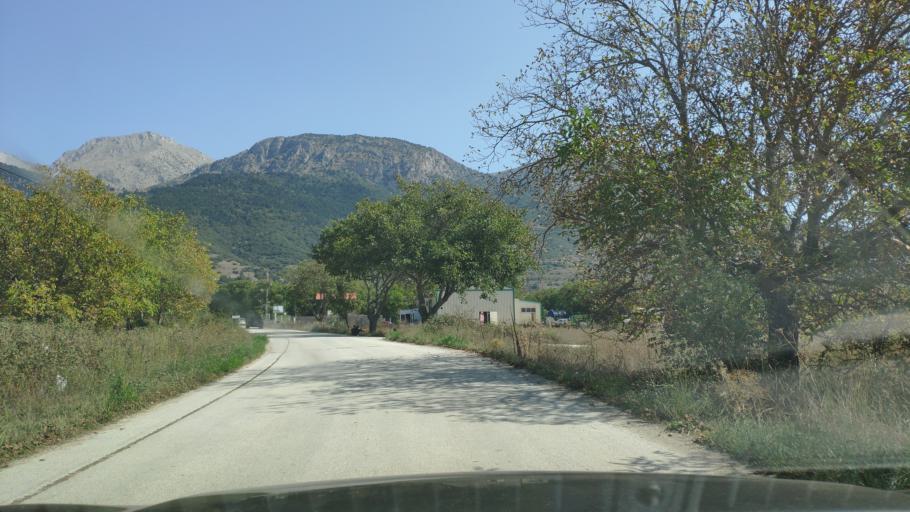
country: GR
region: West Greece
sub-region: Nomos Achaias
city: Kalavryta
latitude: 37.9080
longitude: 22.3194
